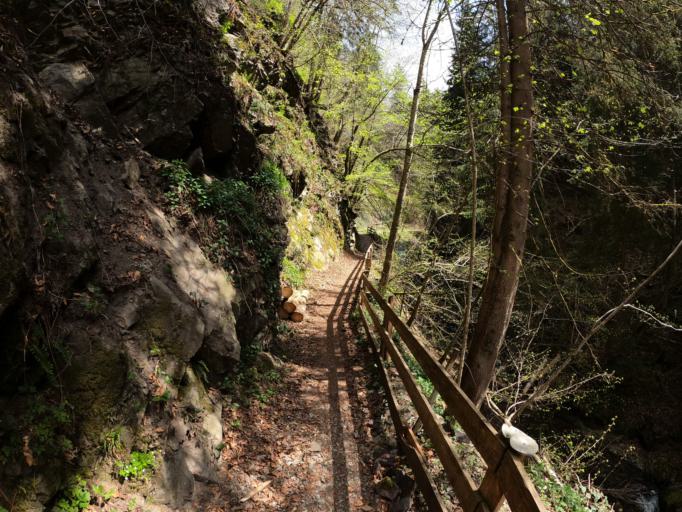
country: AT
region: Salzburg
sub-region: Politischer Bezirk Sankt Johann im Pongau
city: Pfarrwerfen
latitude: 47.4625
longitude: 13.2075
